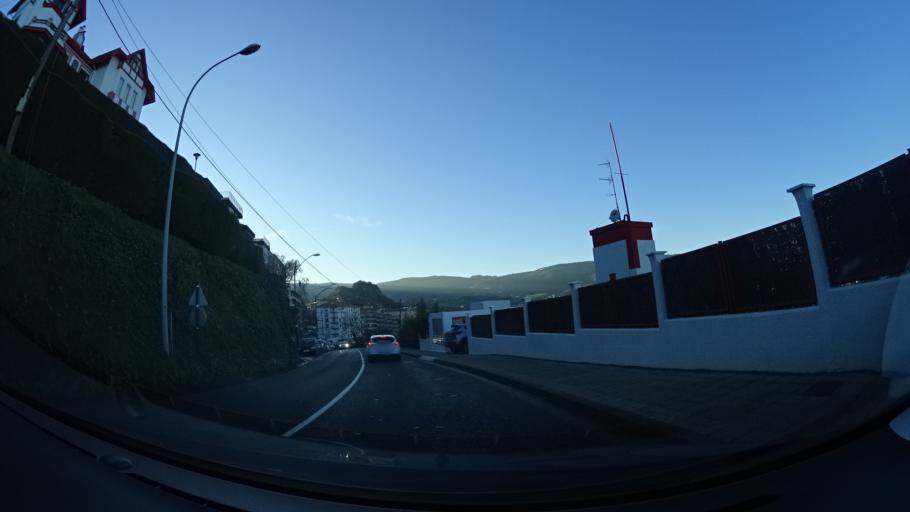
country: ES
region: Basque Country
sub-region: Bizkaia
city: Bermeo
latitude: 43.4169
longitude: -2.7183
